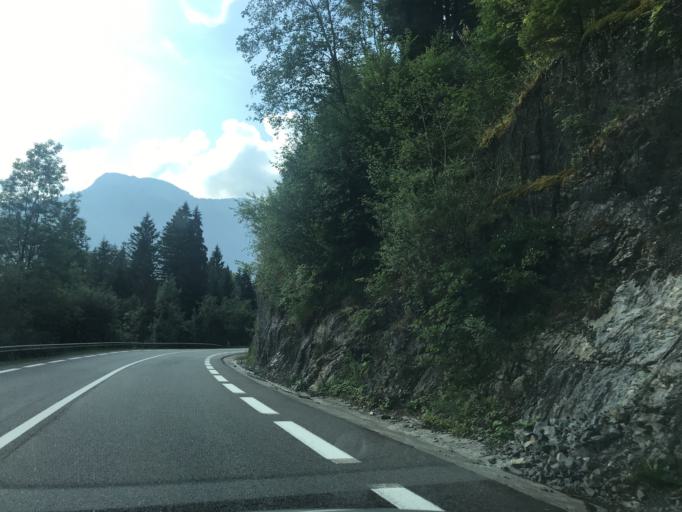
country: FR
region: Rhone-Alpes
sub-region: Departement de la Haute-Savoie
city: Dingy-Saint-Clair
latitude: 45.9009
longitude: 6.2120
